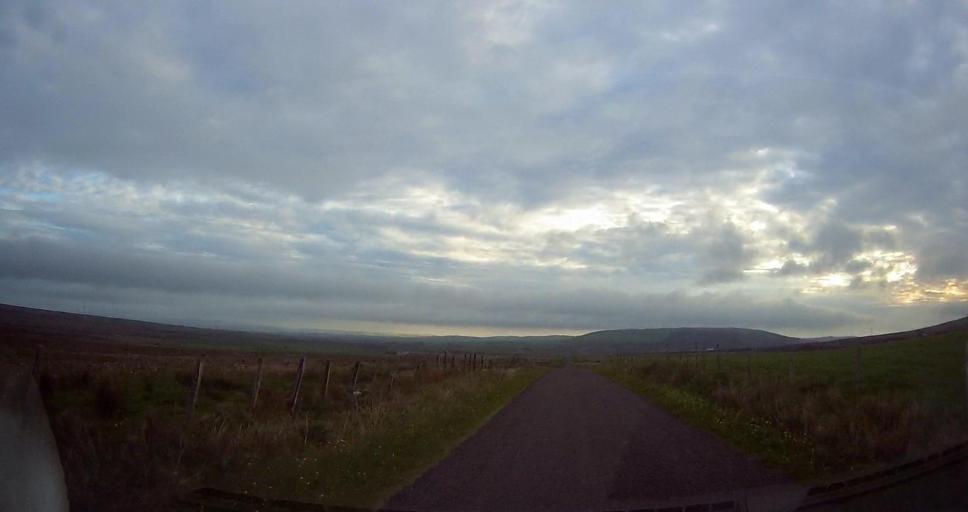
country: GB
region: Scotland
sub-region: Orkney Islands
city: Stromness
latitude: 59.0949
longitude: -3.1660
